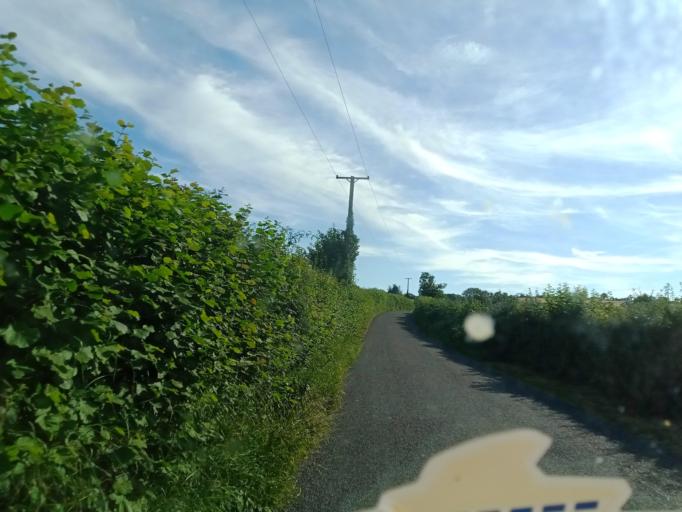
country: IE
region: Leinster
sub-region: Kilkenny
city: Ballyragget
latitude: 52.7727
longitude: -7.3885
